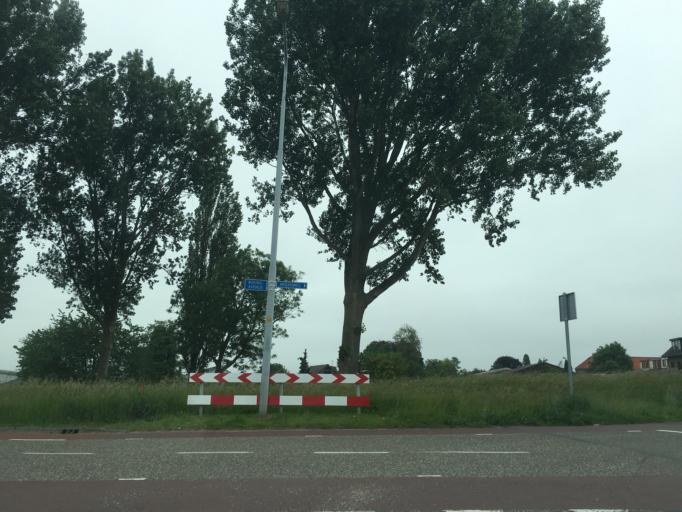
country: NL
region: North Holland
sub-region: Gemeente Aalsmeer
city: Aalsmeer
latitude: 52.2749
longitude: 4.7552
